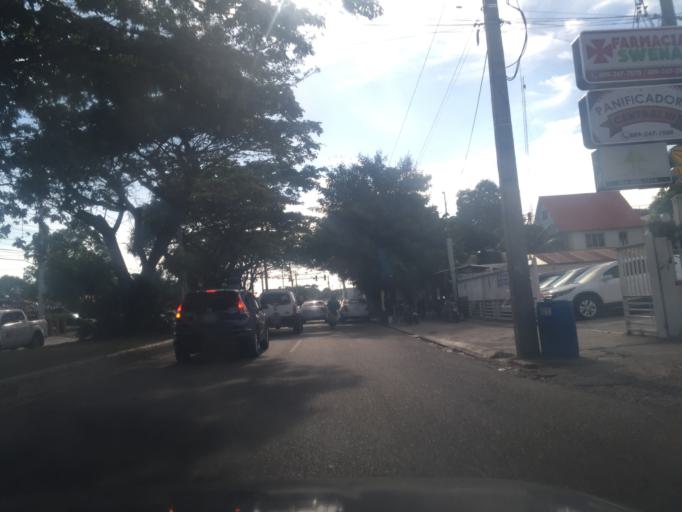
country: DO
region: Santiago
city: Santiago de los Caballeros
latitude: 19.4396
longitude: -70.7216
